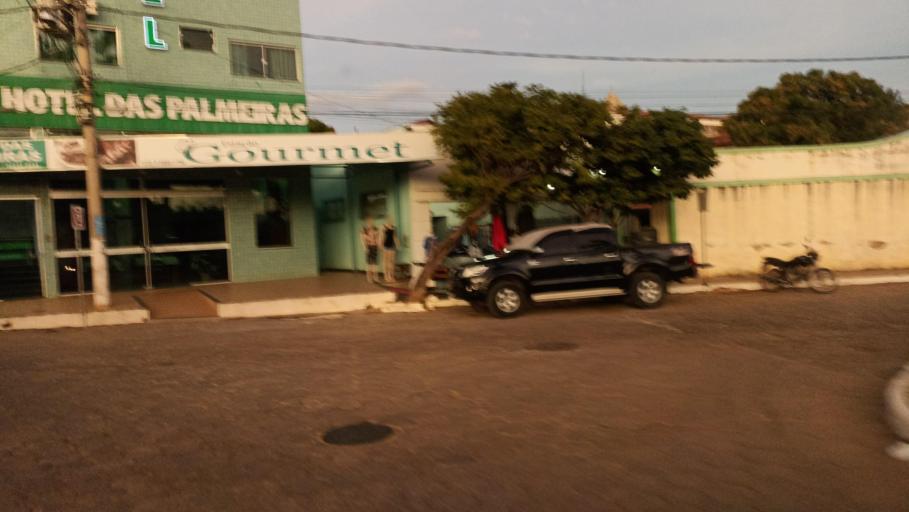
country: BR
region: Minas Gerais
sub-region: Aracuai
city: Aracuai
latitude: -16.6182
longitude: -42.1828
